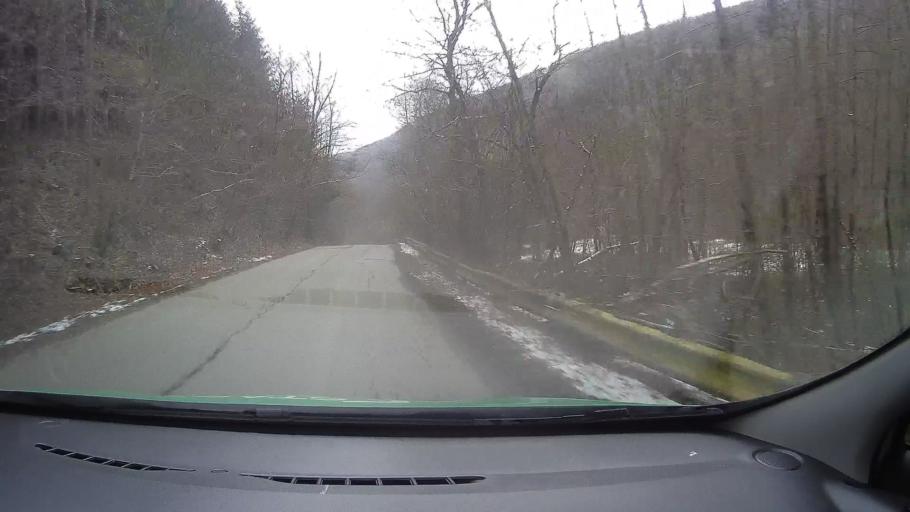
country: RO
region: Hunedoara
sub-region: Comuna Balsa
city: Balsa
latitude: 46.0001
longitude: 23.1502
